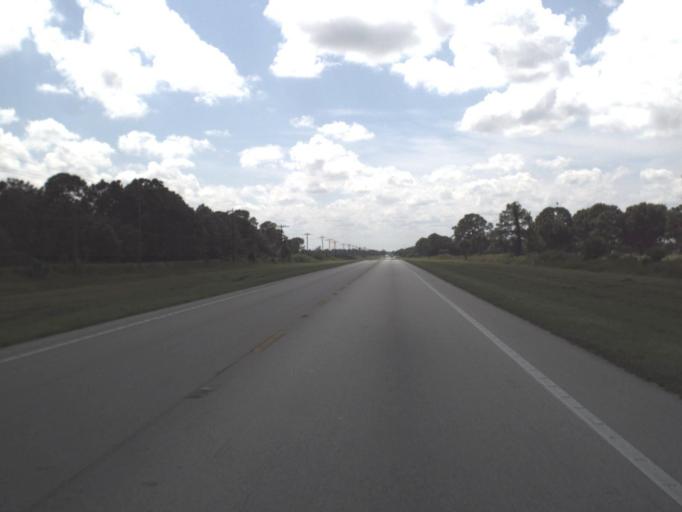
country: US
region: Florida
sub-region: Collier County
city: Immokalee
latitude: 26.4685
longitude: -81.4344
